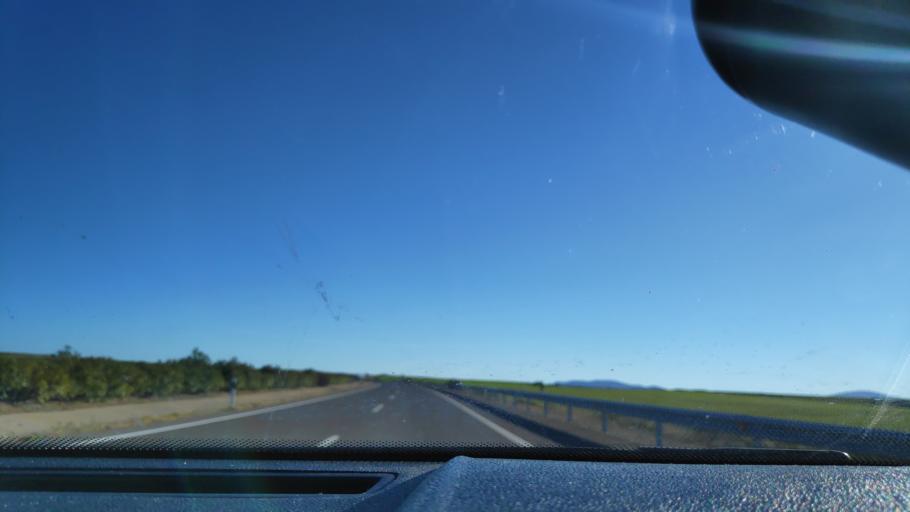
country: ES
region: Extremadura
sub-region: Provincia de Badajoz
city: Fuente de Cantos
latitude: 38.1991
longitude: -6.2848
